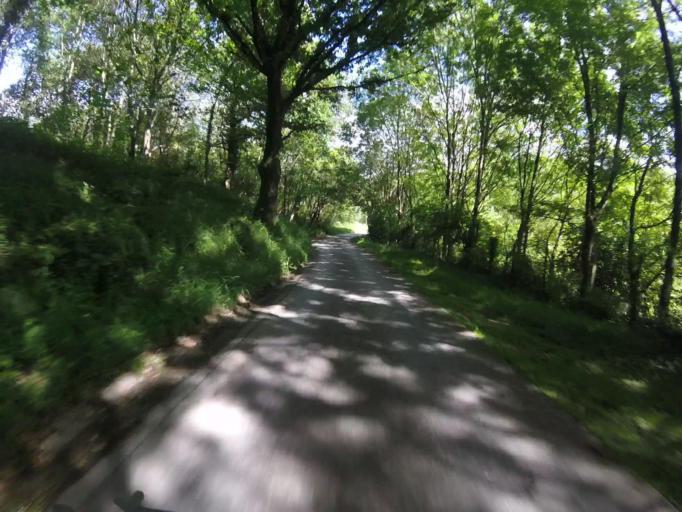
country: ES
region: Basque Country
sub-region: Provincia de Guipuzcoa
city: Errenteria
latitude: 43.2933
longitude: -1.9124
